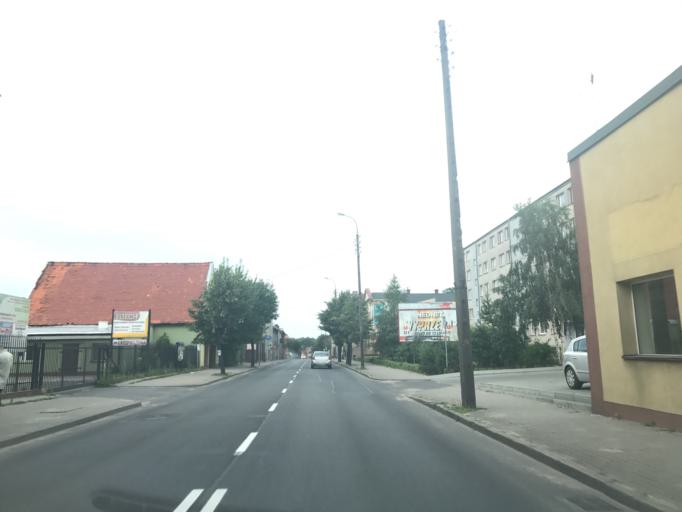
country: PL
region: Kujawsko-Pomorskie
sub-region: Powiat lipnowski
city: Lipno
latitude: 52.8422
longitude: 19.1771
